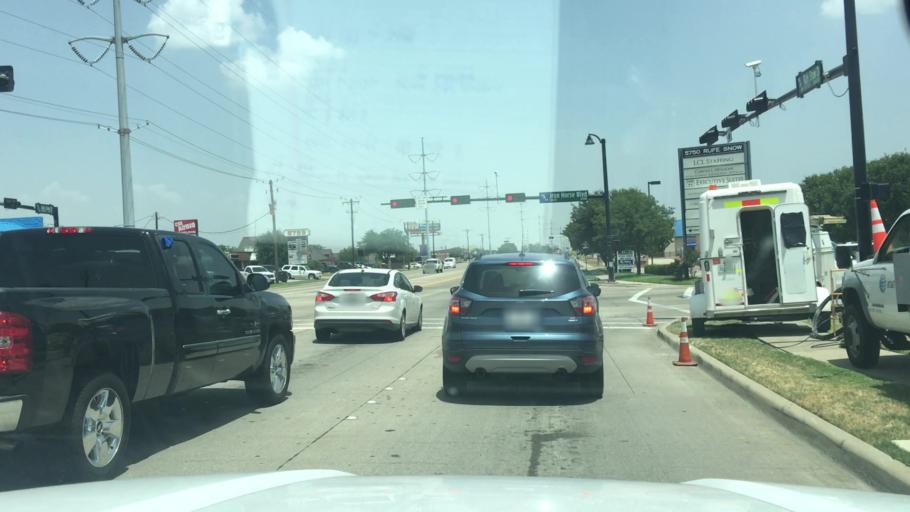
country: US
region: Texas
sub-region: Tarrant County
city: Watauga
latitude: 32.8511
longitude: -97.2385
